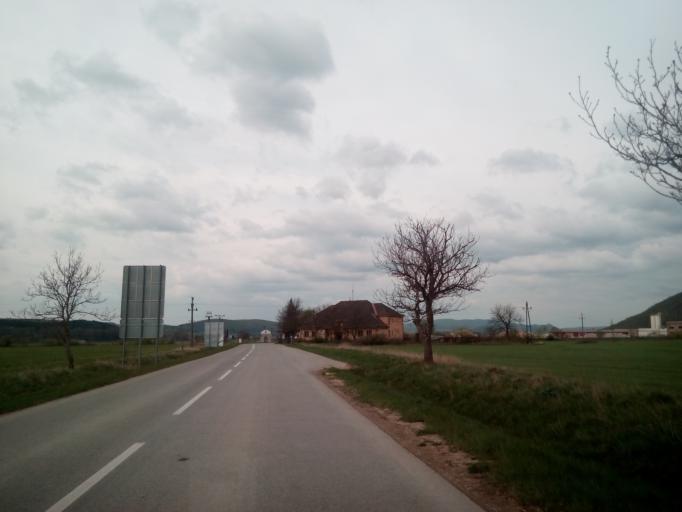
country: SK
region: Kosicky
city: Medzev
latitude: 48.5833
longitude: 20.8513
